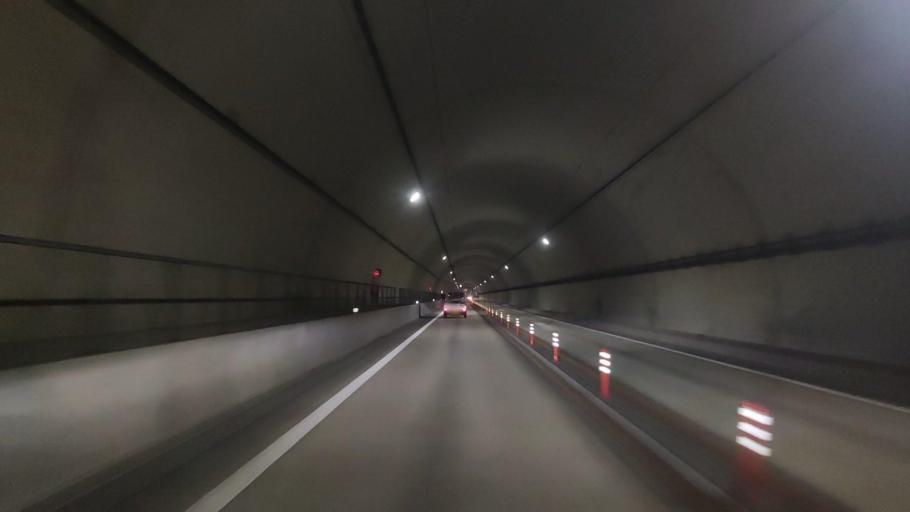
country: JP
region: Wakayama
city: Tanabe
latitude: 33.6020
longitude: 135.4312
